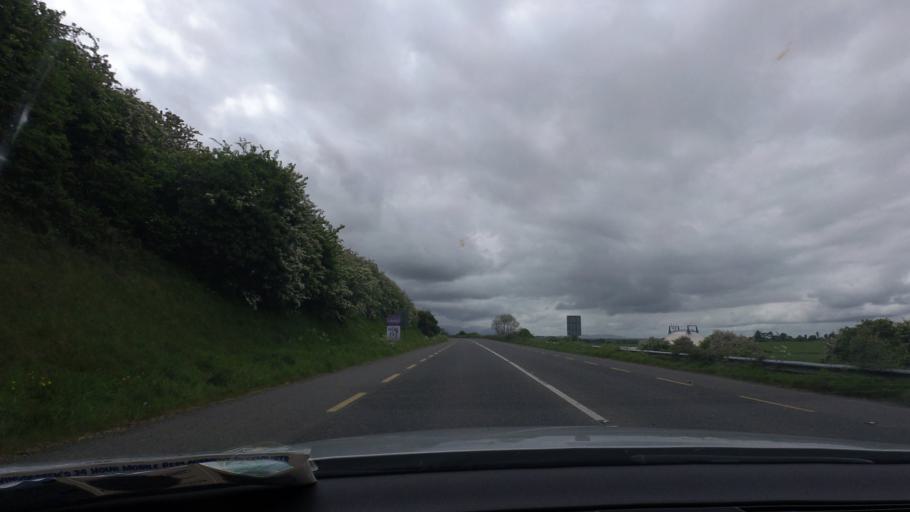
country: IE
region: Munster
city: Cashel
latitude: 52.5258
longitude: -7.8839
